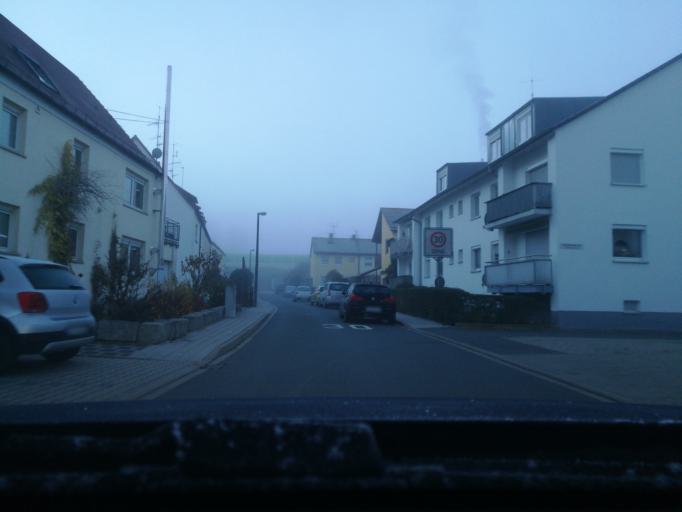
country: DE
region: Bavaria
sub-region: Regierungsbezirk Mittelfranken
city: Veitsbronn
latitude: 49.5074
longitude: 10.8825
